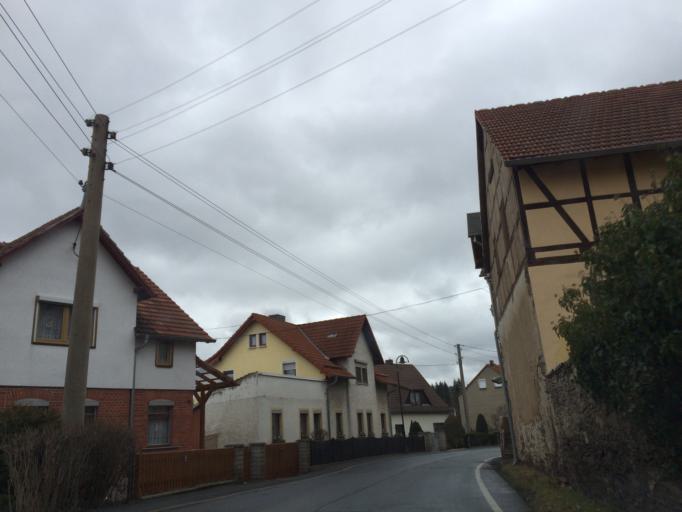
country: DE
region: Thuringia
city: Wernburg
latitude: 50.6766
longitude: 11.6048
